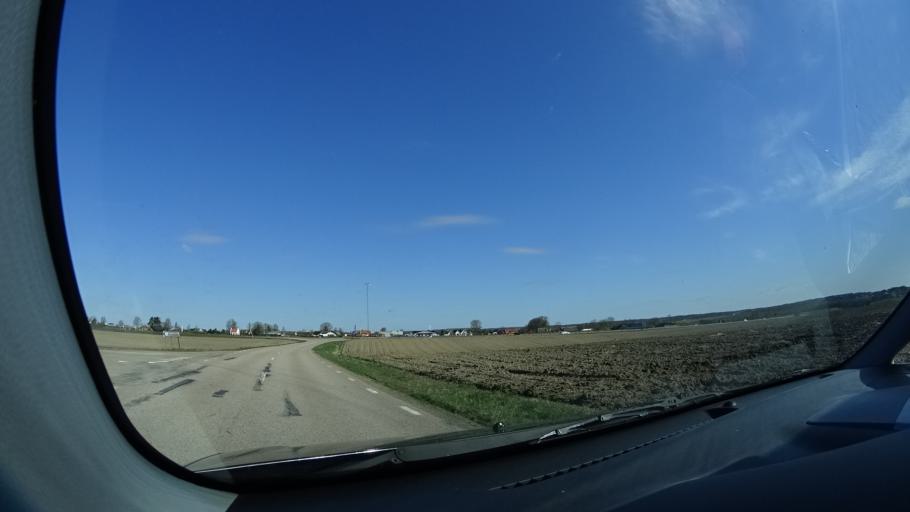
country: SE
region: Skane
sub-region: Astorps Kommun
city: Kvidinge
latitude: 56.1241
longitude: 13.0788
